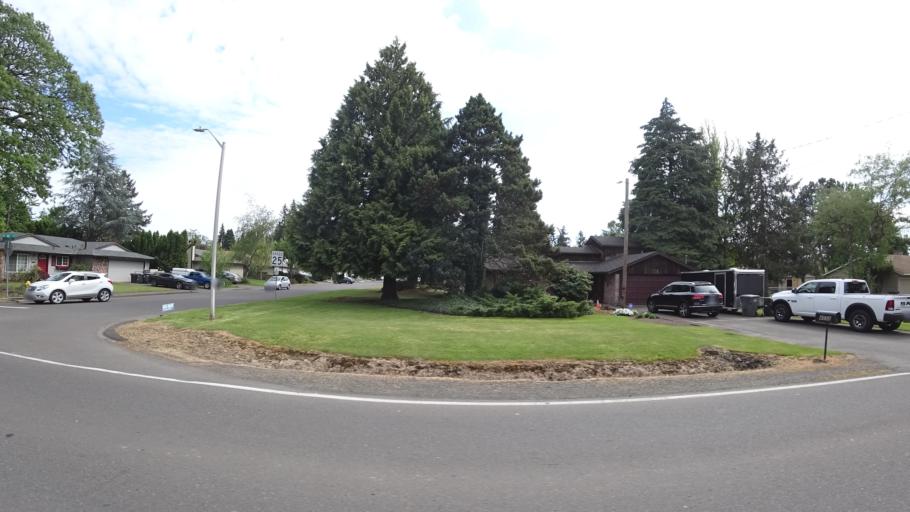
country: US
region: Oregon
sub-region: Washington County
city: Hillsboro
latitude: 45.4997
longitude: -122.9362
